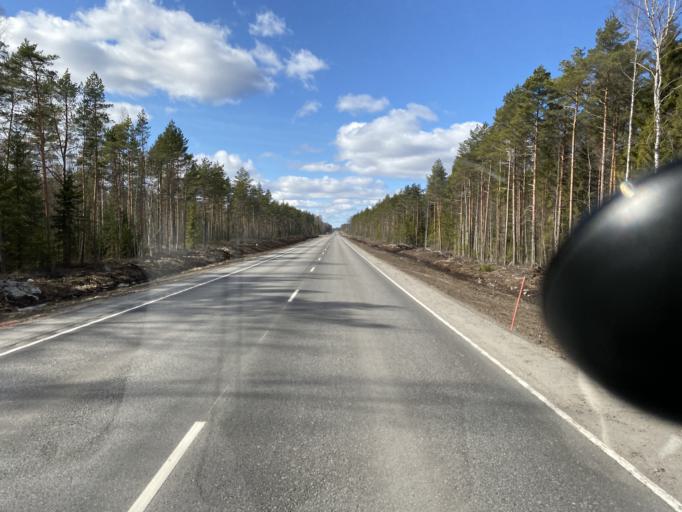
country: FI
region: Satakunta
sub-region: Pori
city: Huittinen
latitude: 61.1745
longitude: 22.5576
